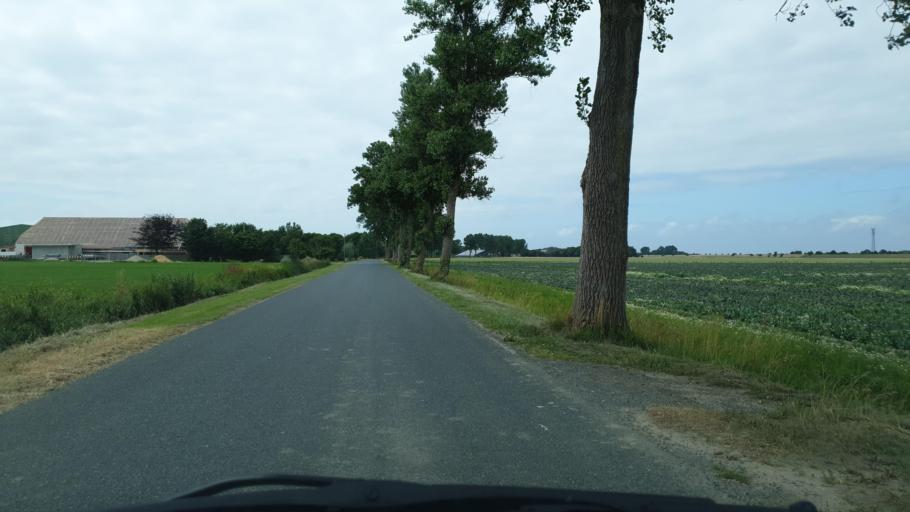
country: DE
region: Schleswig-Holstein
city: Friedrichskoog
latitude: 54.0071
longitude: 8.8703
